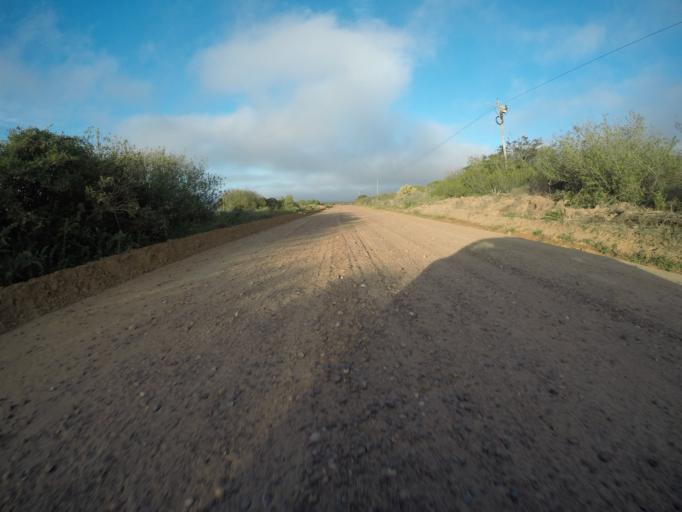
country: ZA
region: Western Cape
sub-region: Eden District Municipality
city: Mossel Bay
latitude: -34.1436
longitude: 22.0233
